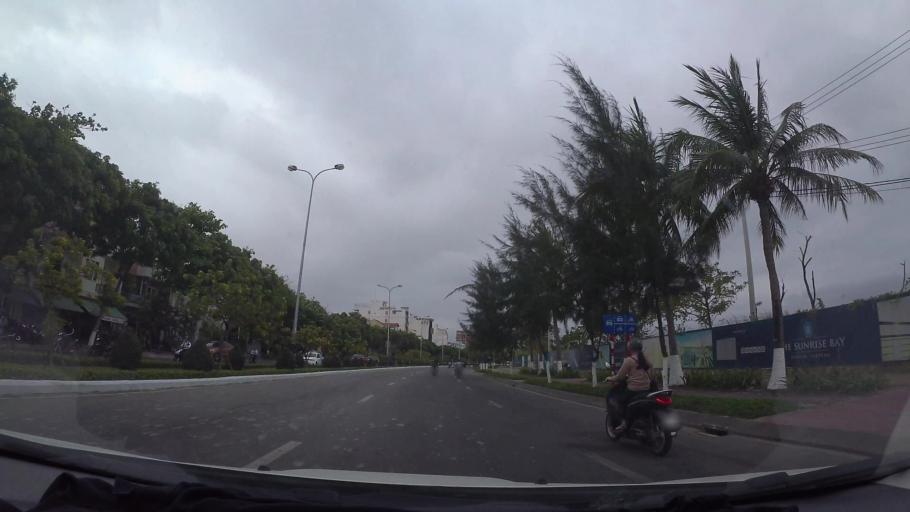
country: VN
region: Da Nang
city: Da Nang
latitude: 16.0829
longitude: 108.2129
